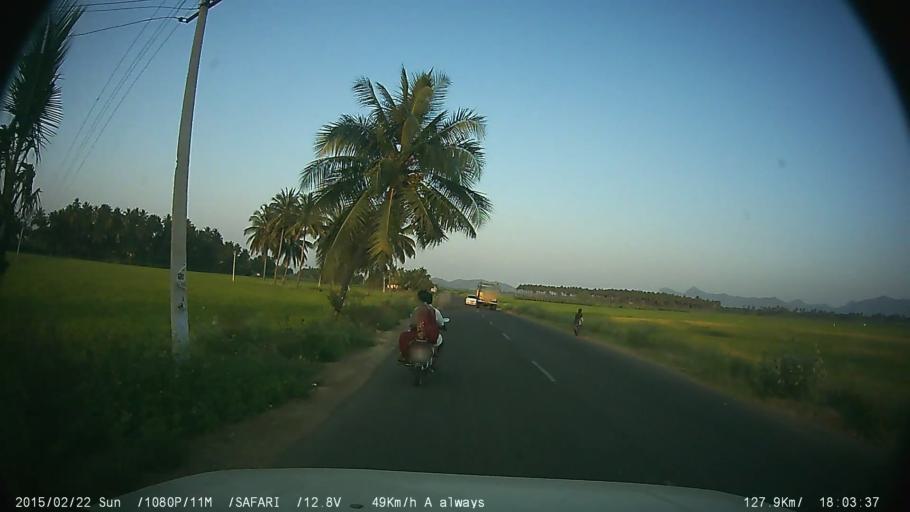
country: IN
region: Tamil Nadu
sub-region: Theni
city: Uttamapalaiyam
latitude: 9.8112
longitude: 77.3444
